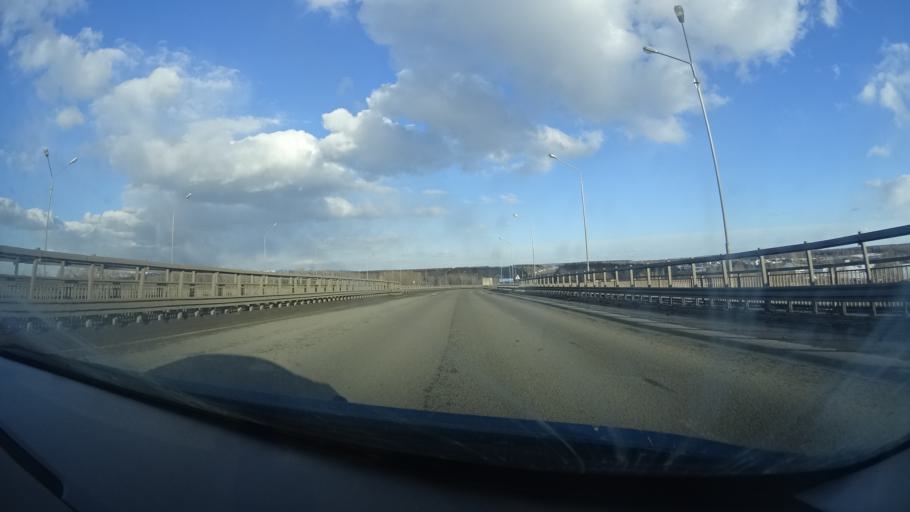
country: RU
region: Bashkortostan
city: Avdon
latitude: 54.6758
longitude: 55.8116
